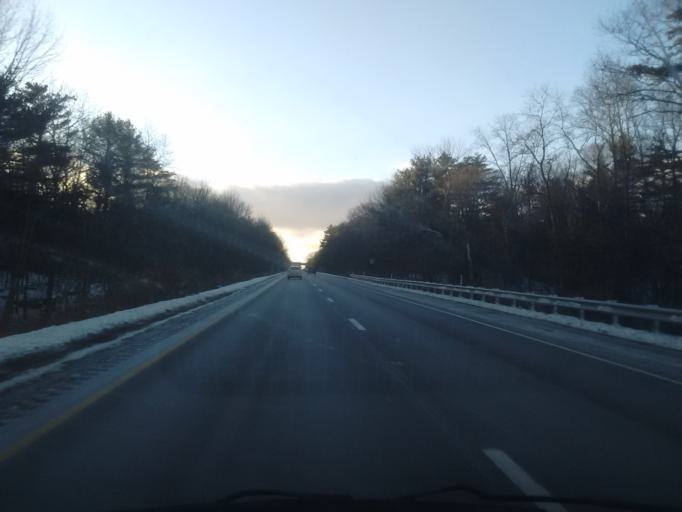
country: US
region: Pennsylvania
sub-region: Pike County
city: Gold Key Lake
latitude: 41.3415
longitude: -74.8974
